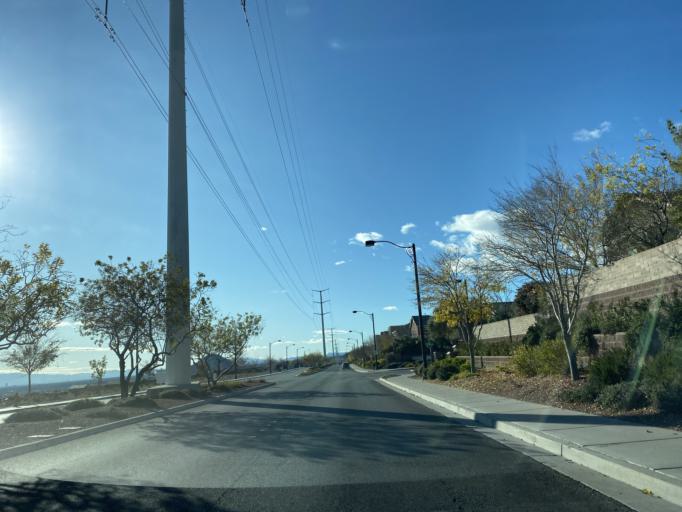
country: US
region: Nevada
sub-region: Clark County
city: Summerlin South
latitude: 36.2843
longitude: -115.3289
